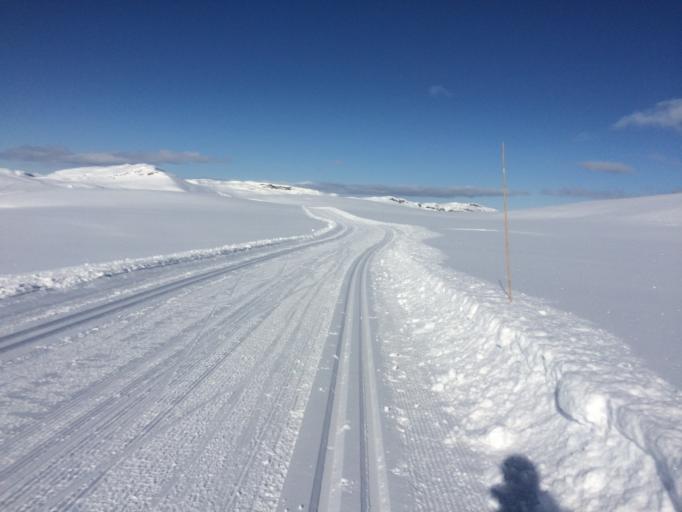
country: NO
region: Oppland
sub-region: Ringebu
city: Ringebu
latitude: 61.3546
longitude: 10.0869
